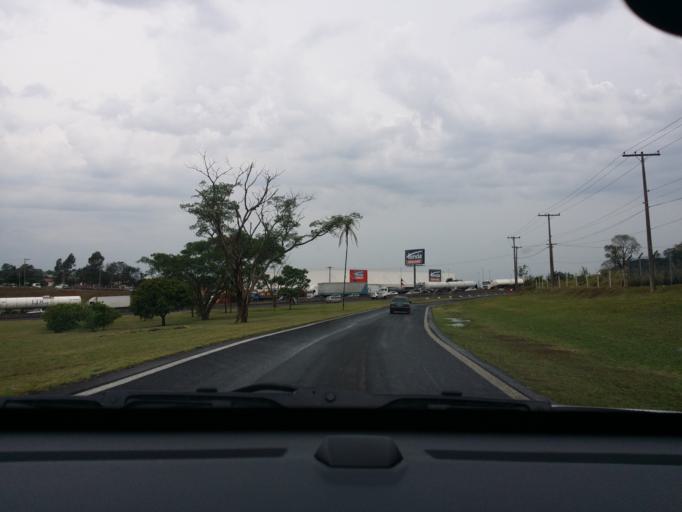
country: BR
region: Sao Paulo
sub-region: Sao Carlos
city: Sao Carlos
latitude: -22.0365
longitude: -47.8621
